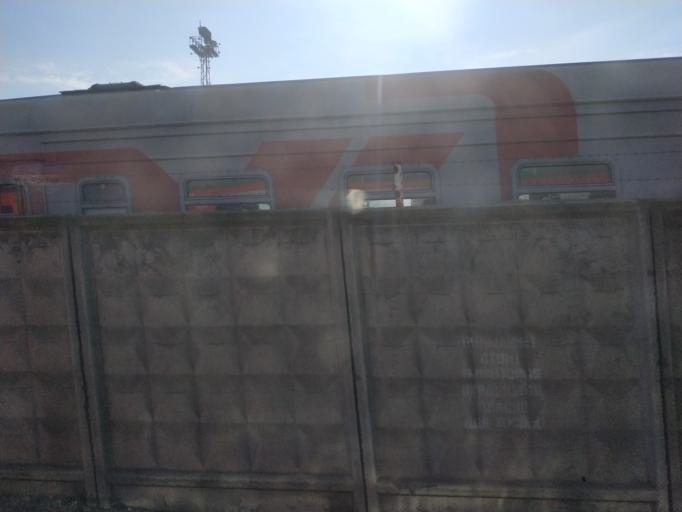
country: RU
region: Volgograd
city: Volgograd
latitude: 48.7154
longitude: 44.5172
